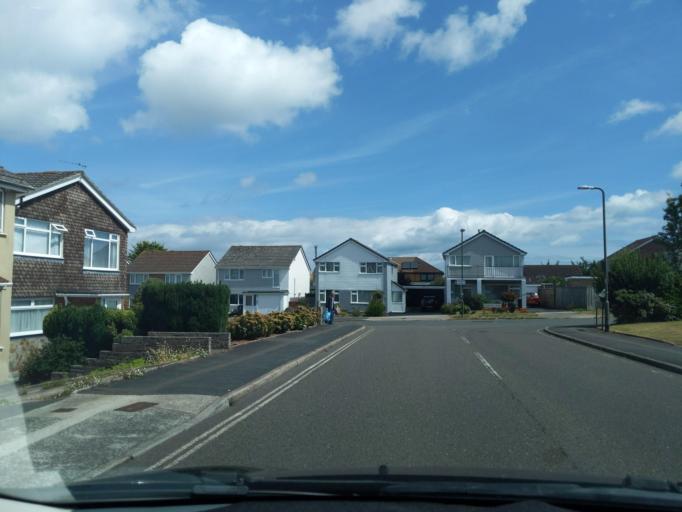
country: GB
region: England
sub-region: Borough of Torbay
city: Paignton
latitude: 50.4104
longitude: -3.5671
